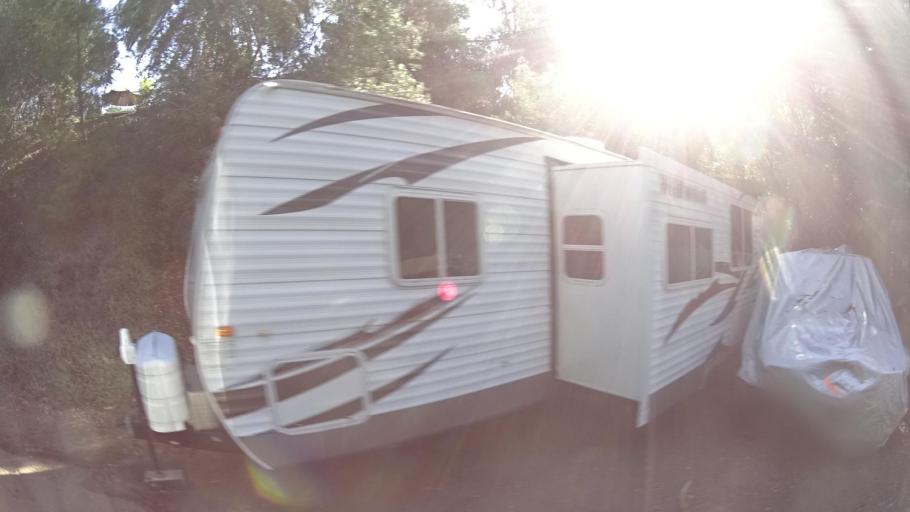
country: US
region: California
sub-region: San Diego County
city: Casa de Oro-Mount Helix
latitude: 32.7707
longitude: -116.9935
